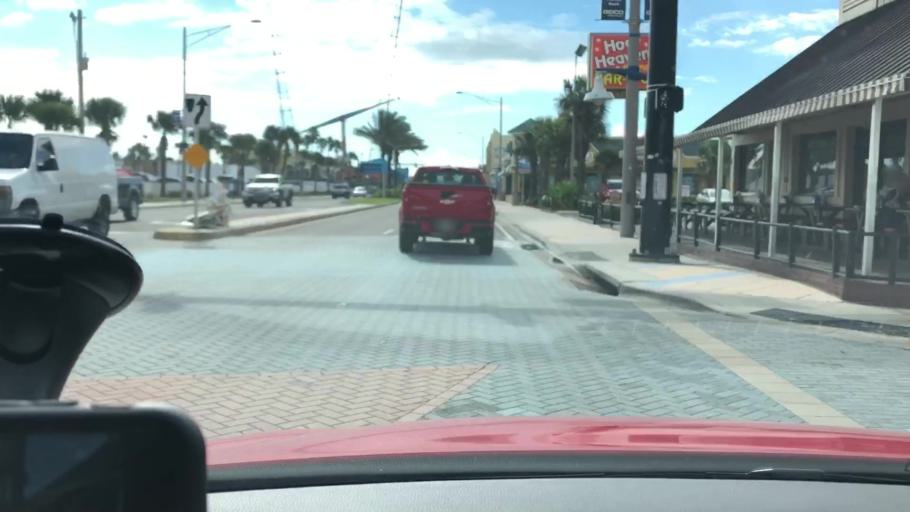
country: US
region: Florida
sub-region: Volusia County
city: Daytona Beach
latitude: 29.2282
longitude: -81.0090
